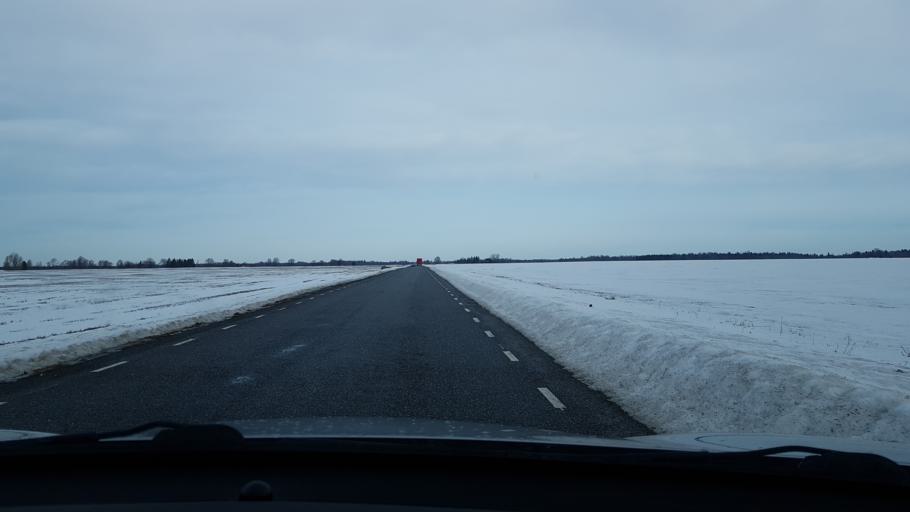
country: EE
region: Jaervamaa
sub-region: Paide linn
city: Paide
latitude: 58.8713
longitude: 25.6695
